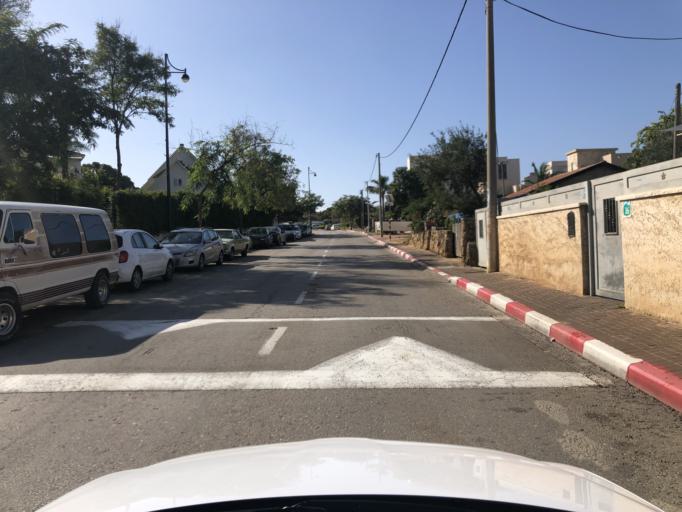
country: IL
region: Central District
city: Ness Ziona
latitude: 31.9121
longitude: 34.7912
